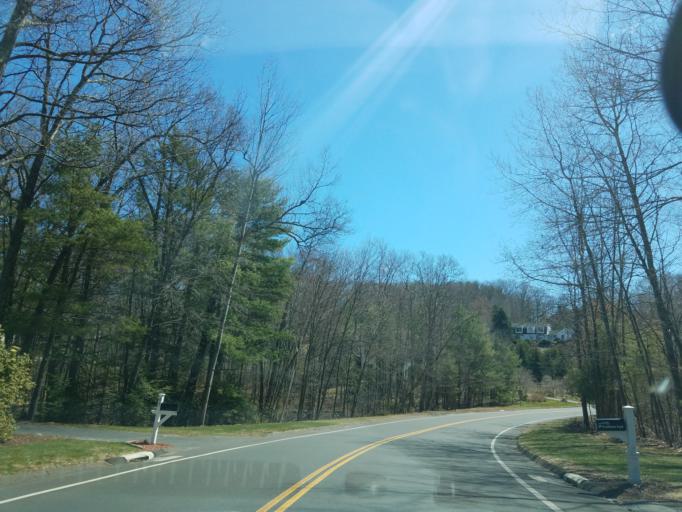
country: US
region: Connecticut
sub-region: Hartford County
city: Canton Valley
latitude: 41.8076
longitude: -72.8696
